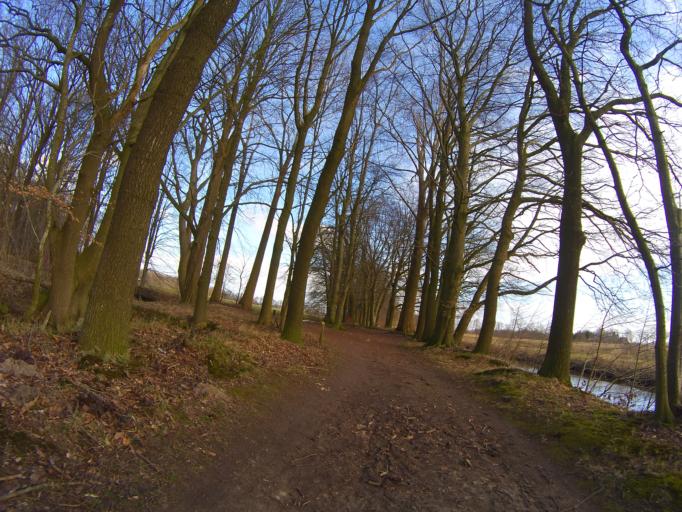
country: NL
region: Utrecht
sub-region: Gemeente Leusden
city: Leusden
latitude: 52.1529
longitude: 5.4653
